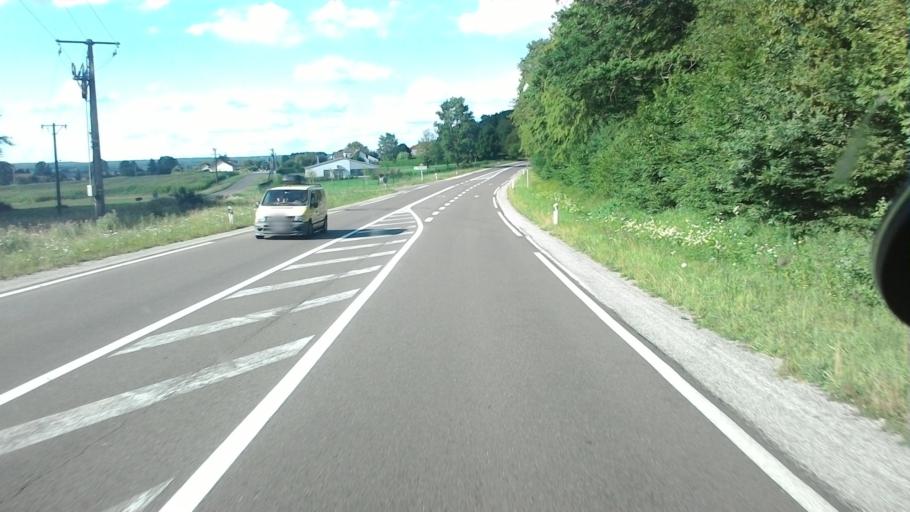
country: FR
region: Franche-Comte
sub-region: Departement de la Haute-Saone
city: Luxeuil-les-Bains
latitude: 47.7666
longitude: 6.3417
